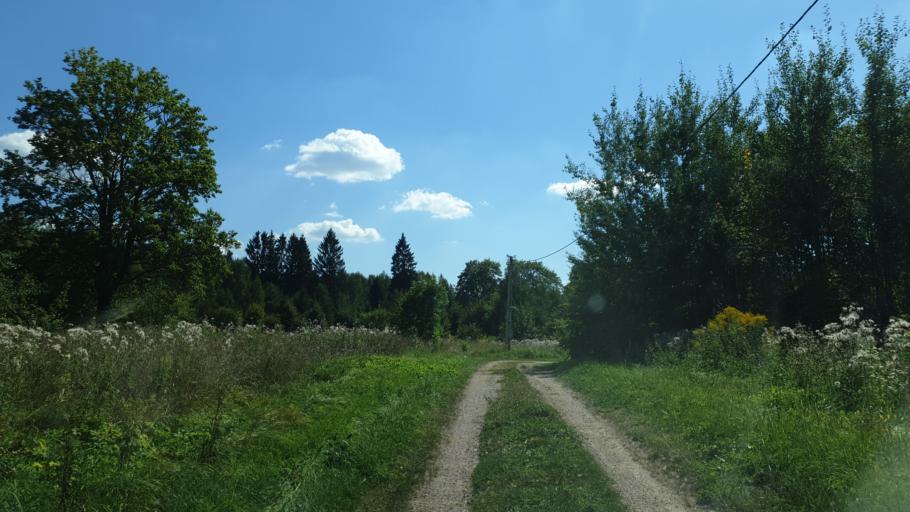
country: LT
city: Sirvintos
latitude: 54.9010
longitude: 24.9115
